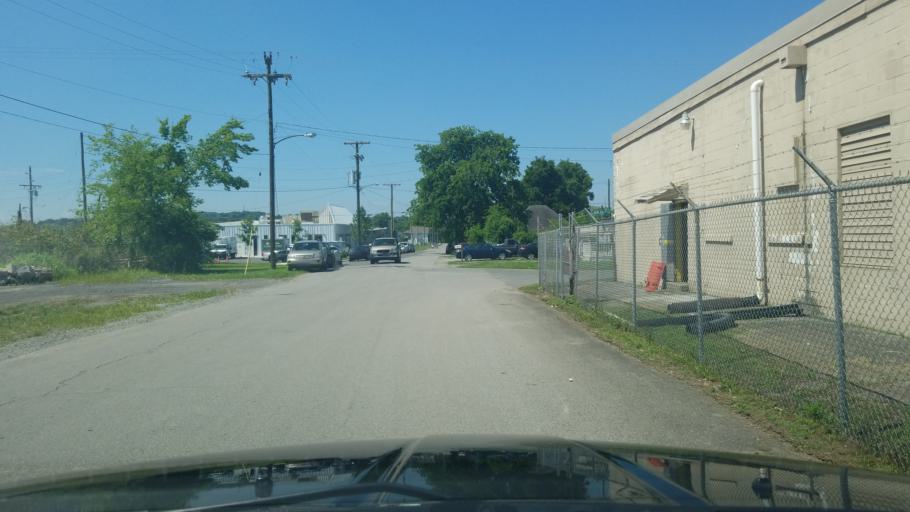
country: US
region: Tennessee
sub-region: Davidson County
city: Belle Meade
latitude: 36.1661
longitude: -86.8581
